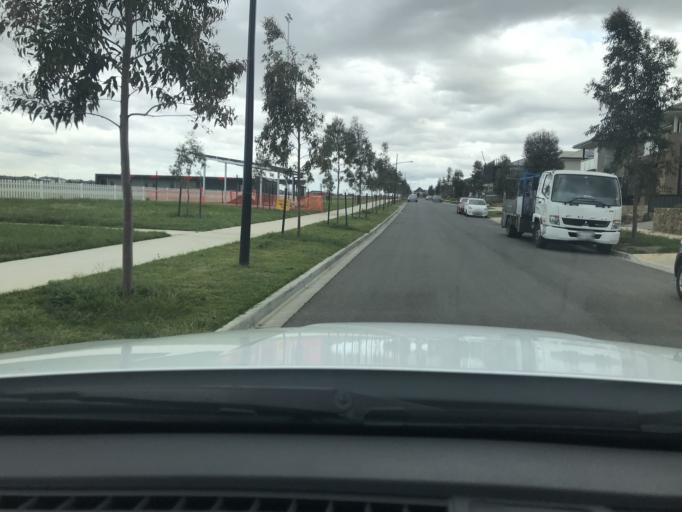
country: AU
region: Victoria
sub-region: Hume
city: Greenvale
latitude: -37.5951
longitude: 144.8902
